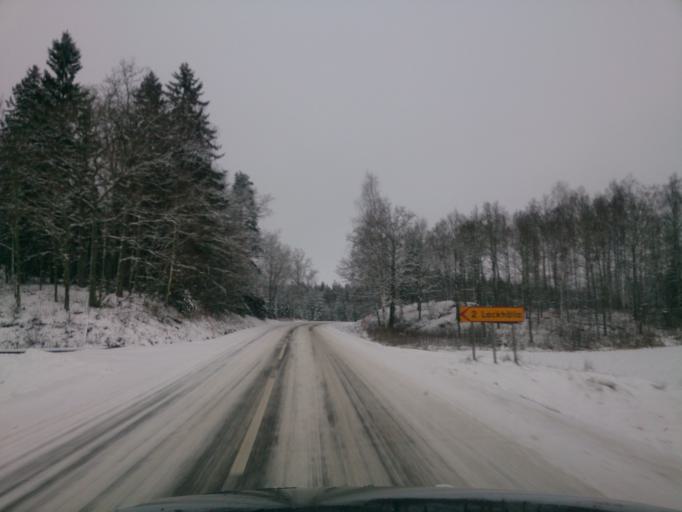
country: SE
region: OEstergoetland
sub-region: Norrkopings Kommun
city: Kimstad
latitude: 58.3718
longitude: 16.0245
